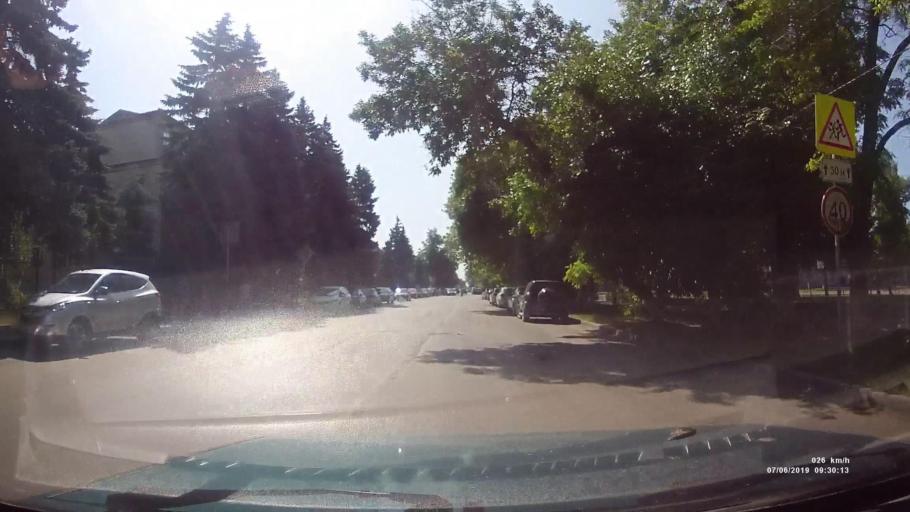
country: RU
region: Rostov
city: Azov
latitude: 47.1058
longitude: 39.4219
